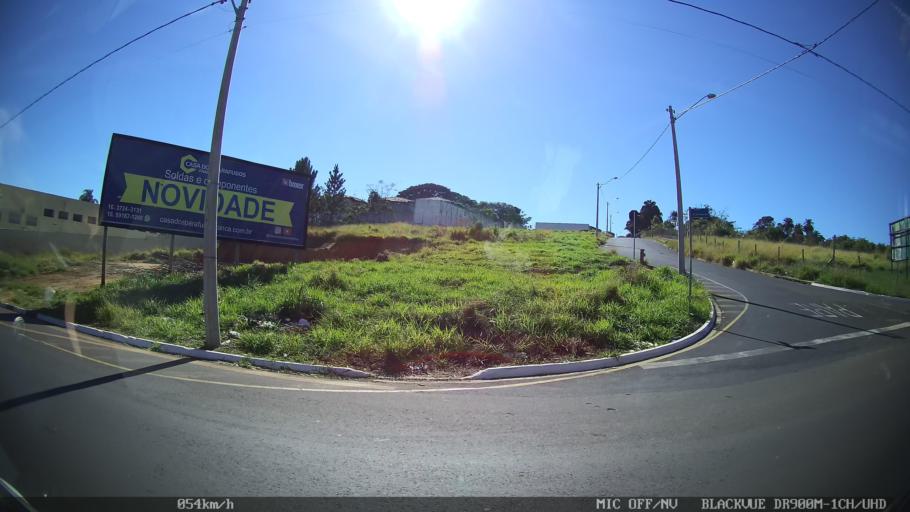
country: BR
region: Sao Paulo
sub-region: Franca
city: Franca
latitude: -20.5223
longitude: -47.3726
